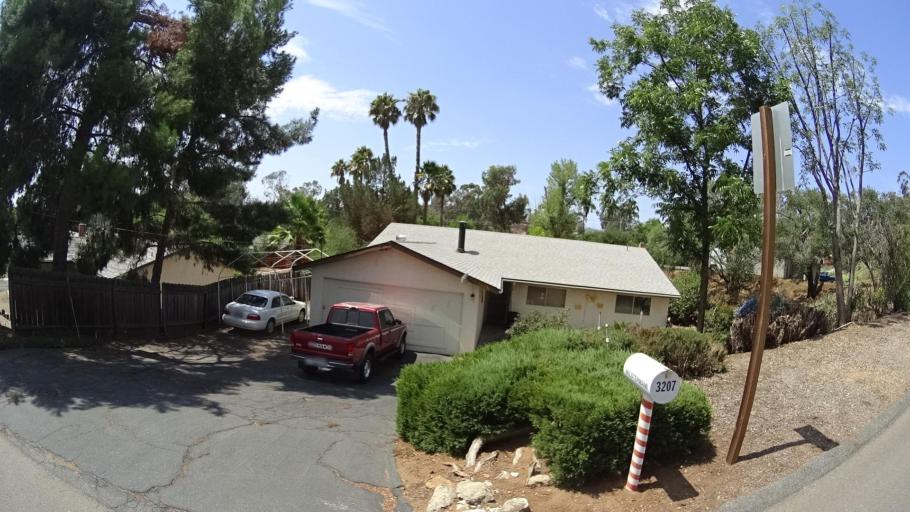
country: US
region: California
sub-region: San Diego County
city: Hidden Meadows
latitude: 33.1796
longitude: -117.0862
